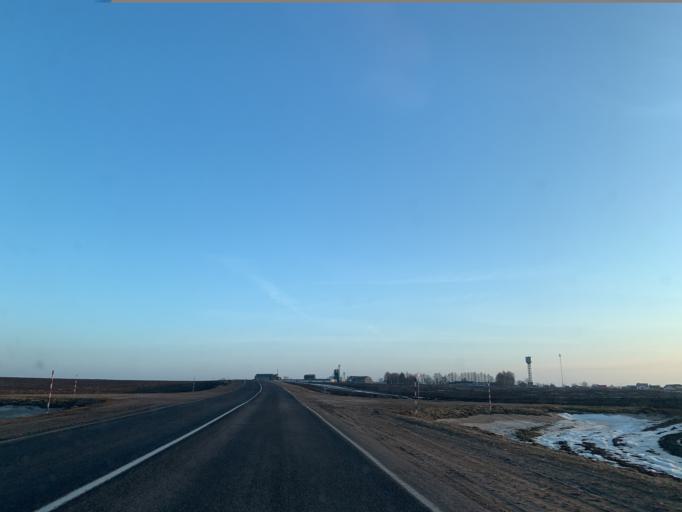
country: BY
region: Minsk
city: Haradzyeya
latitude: 53.3246
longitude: 26.5534
